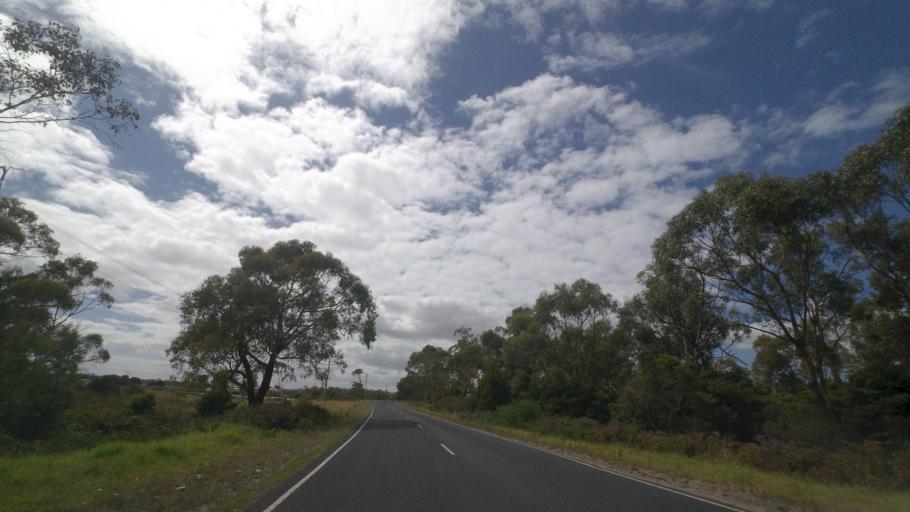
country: AU
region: Victoria
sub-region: Cardinia
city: Koo-Wee-Rup
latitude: -38.2827
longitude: 145.5961
